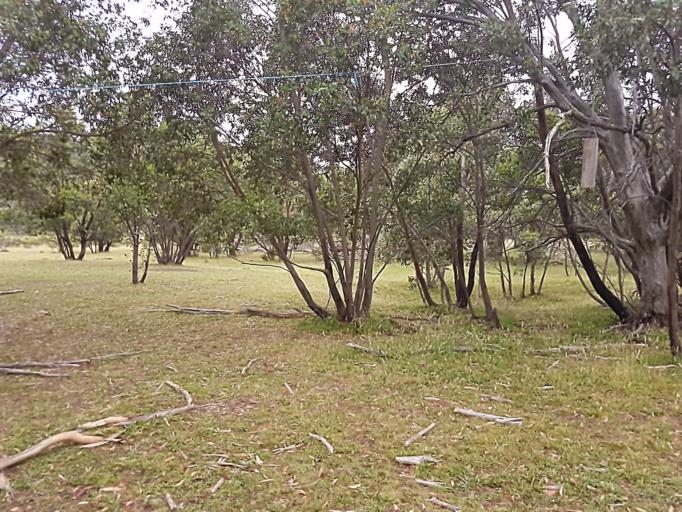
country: AU
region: New South Wales
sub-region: Snowy River
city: Jindabyne
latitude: -36.7980
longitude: 148.1712
